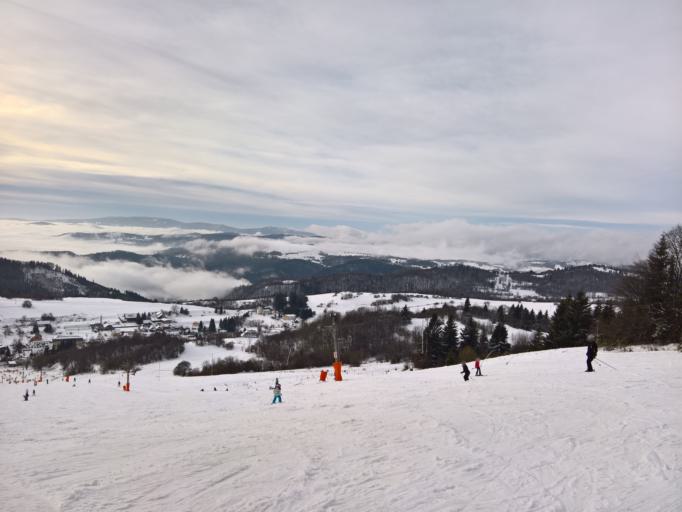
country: SK
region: Banskobystricky
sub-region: Okres Ziar nad Hronom
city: Kremnica
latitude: 48.7296
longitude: 18.9494
